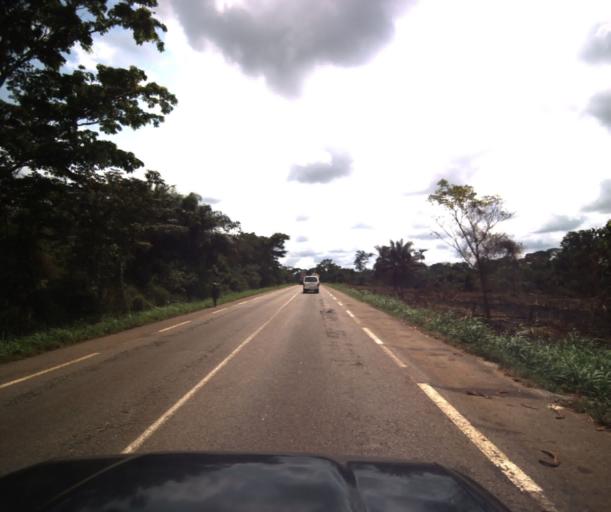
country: CM
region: Centre
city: Eseka
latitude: 3.8604
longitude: 10.5866
